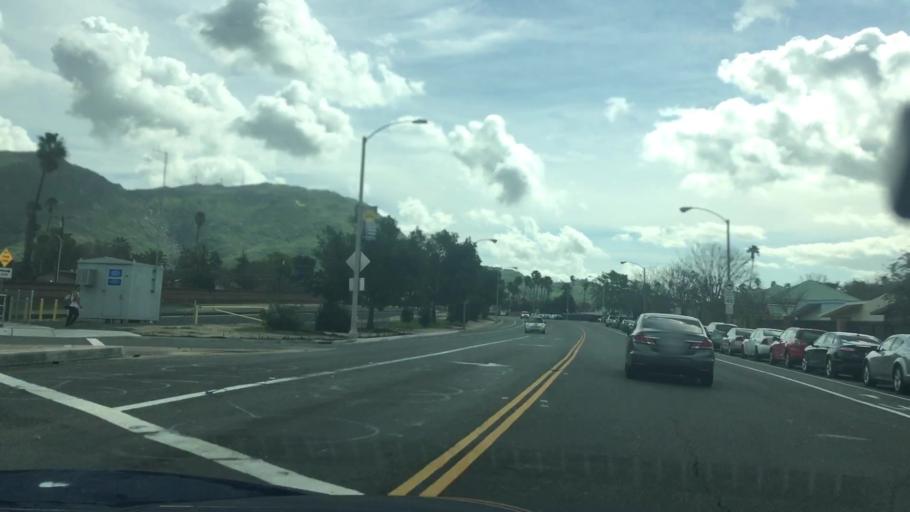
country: US
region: California
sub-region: Riverside County
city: Highgrove
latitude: 33.9828
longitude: -117.3258
